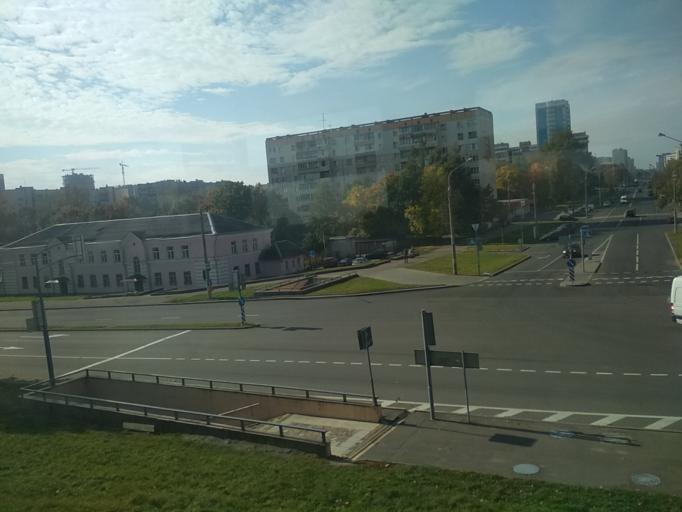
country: BY
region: Minsk
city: Minsk
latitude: 53.8773
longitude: 27.5629
